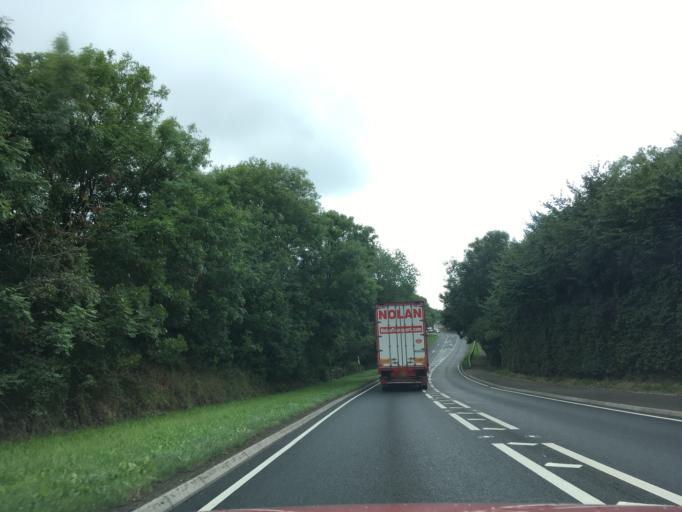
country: GB
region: Wales
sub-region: Pembrokeshire
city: Haverfordwest
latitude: 51.8048
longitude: -4.9496
